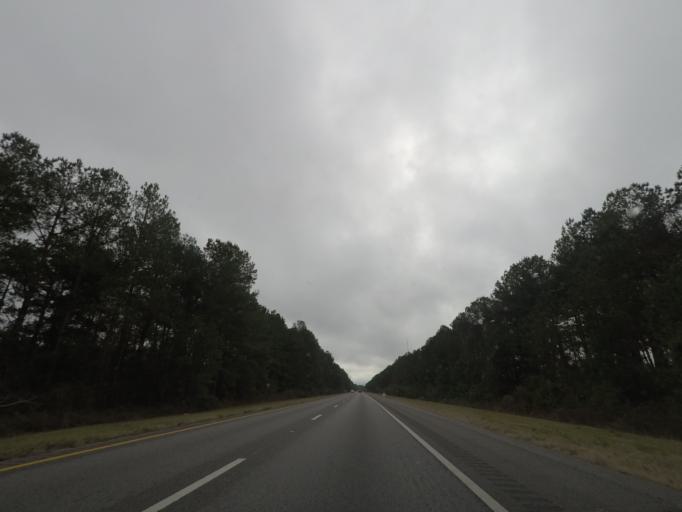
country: US
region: South Carolina
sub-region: Orangeburg County
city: Holly Hill
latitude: 33.3671
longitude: -80.5251
